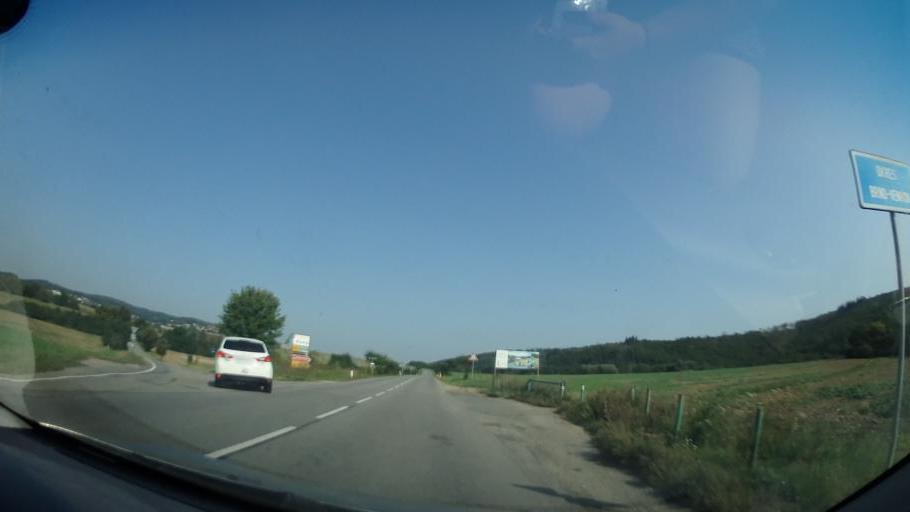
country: CZ
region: South Moravian
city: Kurim
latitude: 49.2408
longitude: 16.5303
